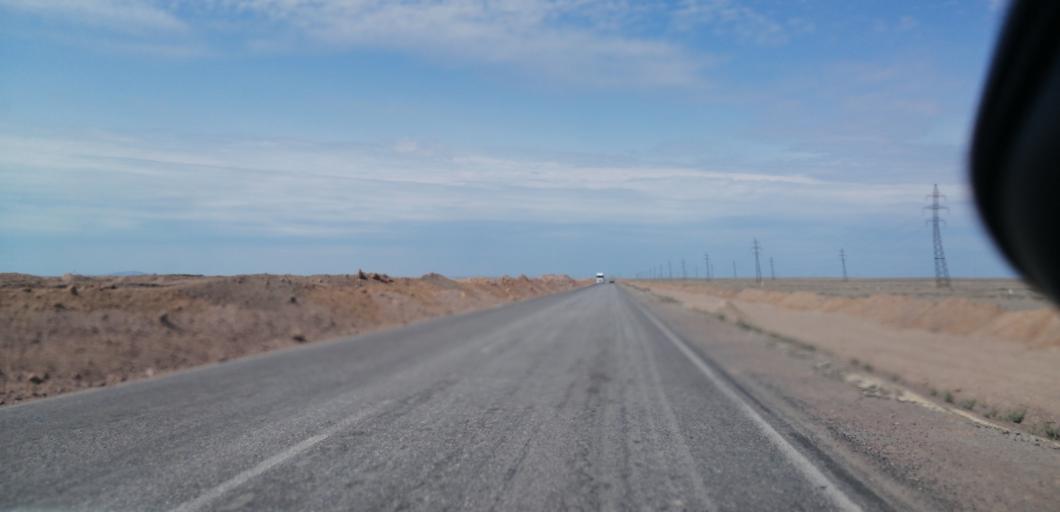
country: KZ
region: Qaraghandy
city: Balqash
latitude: 46.7989
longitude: 74.6727
